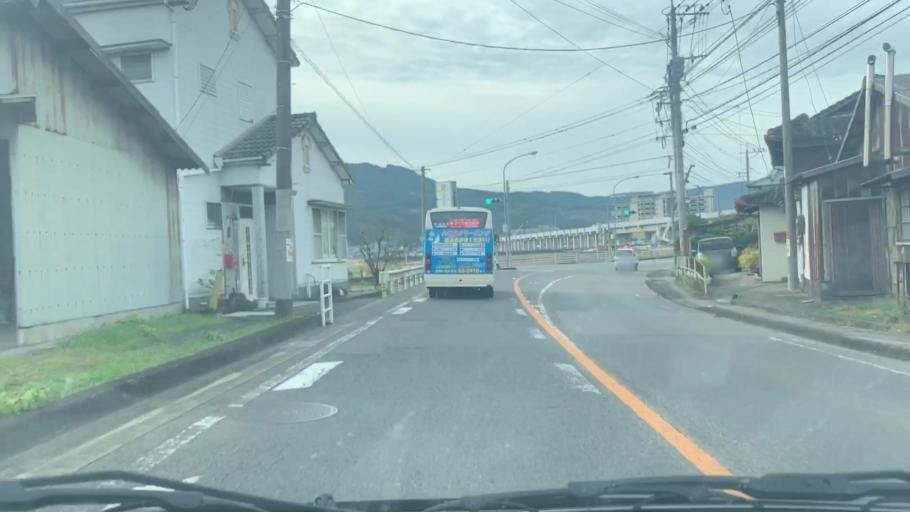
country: JP
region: Saga Prefecture
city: Ureshinomachi-shimojuku
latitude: 33.1107
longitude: 130.0005
